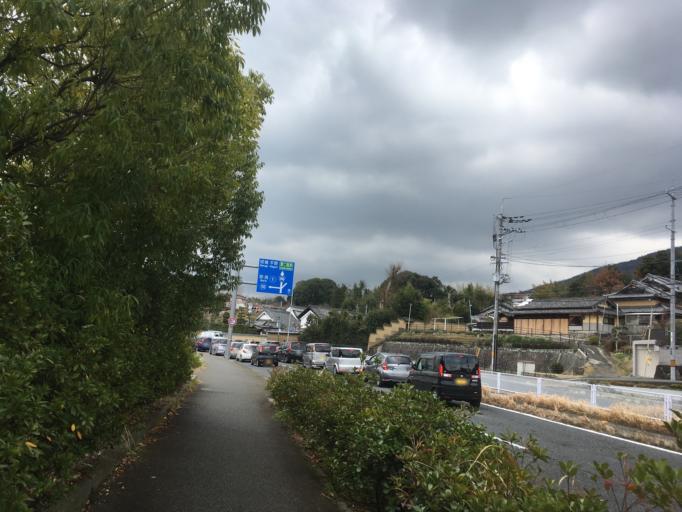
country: JP
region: Nara
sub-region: Ikoma-shi
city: Ikoma
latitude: 34.6860
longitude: 135.7064
